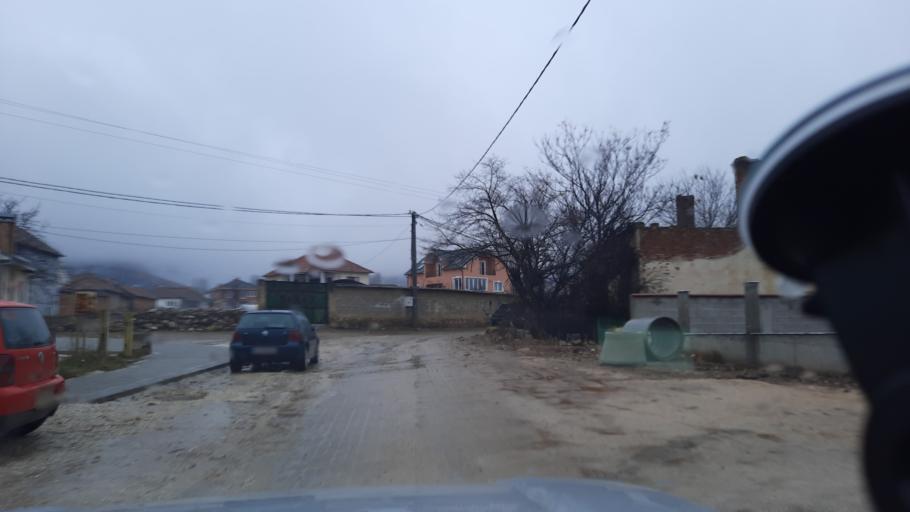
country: MK
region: Opstina Lipkovo
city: Matejche
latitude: 42.1245
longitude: 21.5962
